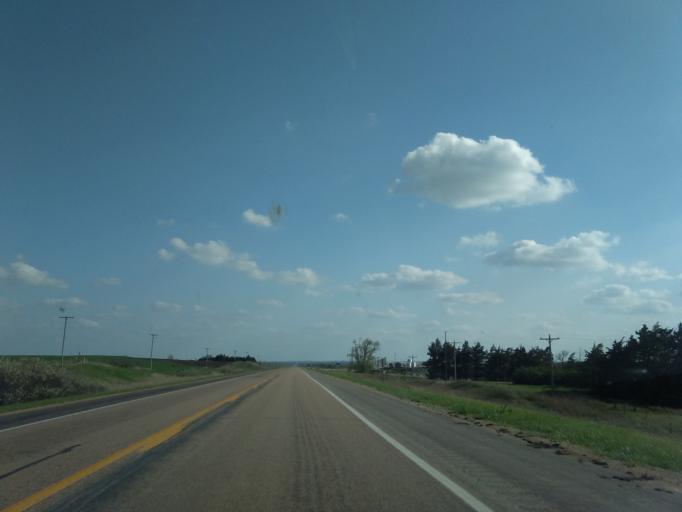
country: US
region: Nebraska
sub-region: Webster County
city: Red Cloud
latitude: 40.1450
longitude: -98.5191
